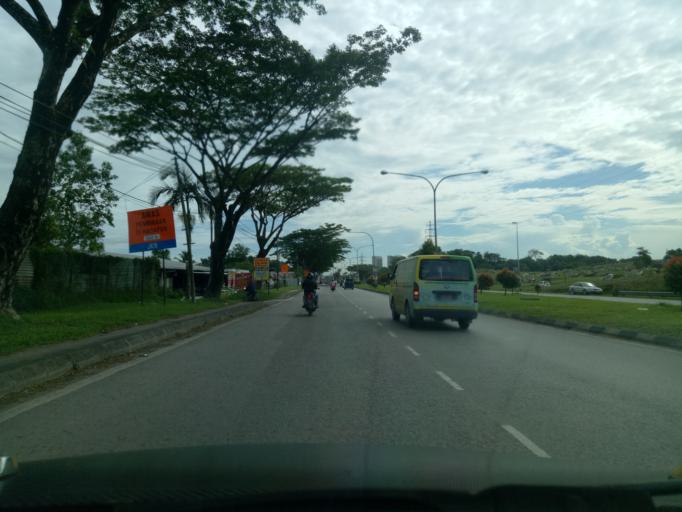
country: MY
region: Sarawak
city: Kuching
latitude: 1.4922
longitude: 110.3307
